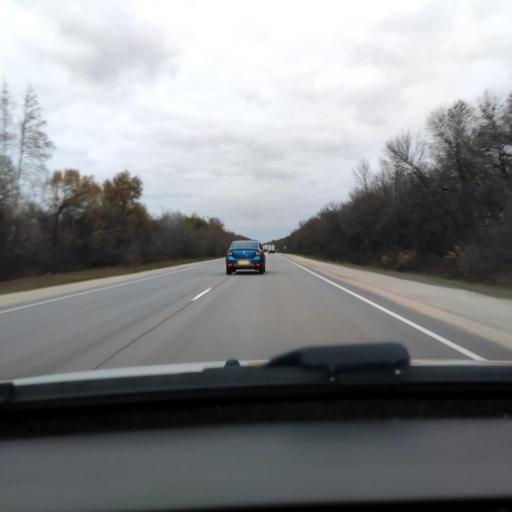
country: RU
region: Lipetsk
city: Borinskoye
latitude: 52.3801
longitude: 39.2183
